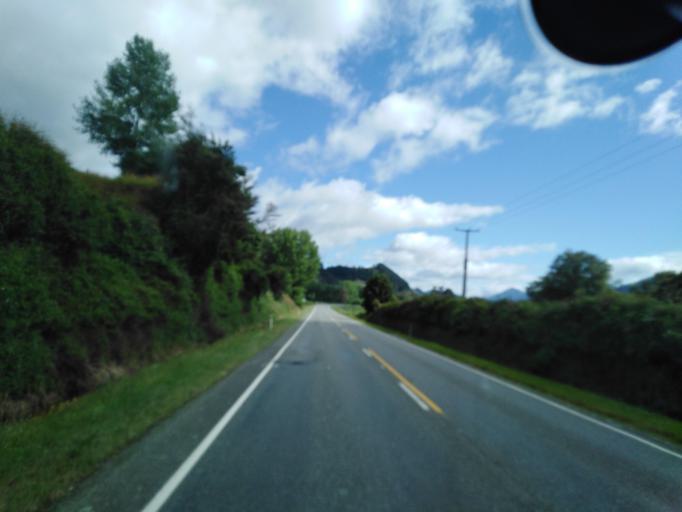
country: NZ
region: Nelson
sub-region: Nelson City
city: Nelson
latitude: -41.2711
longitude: 173.5727
